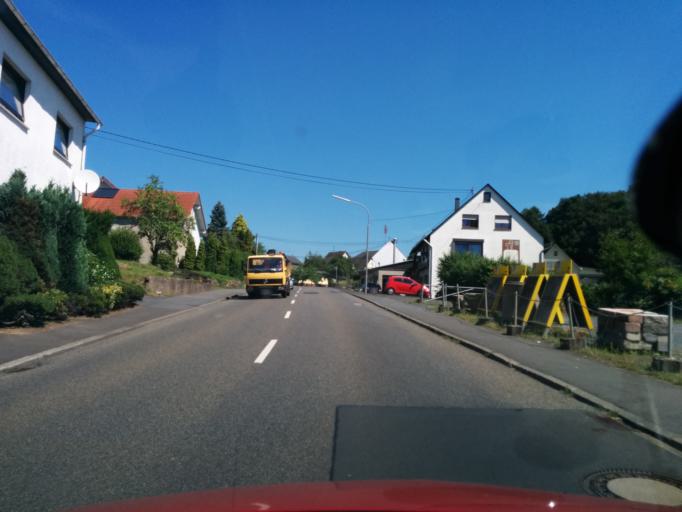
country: DE
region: Rheinland-Pfalz
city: Ettinghausen
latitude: 50.5133
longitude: 7.8726
